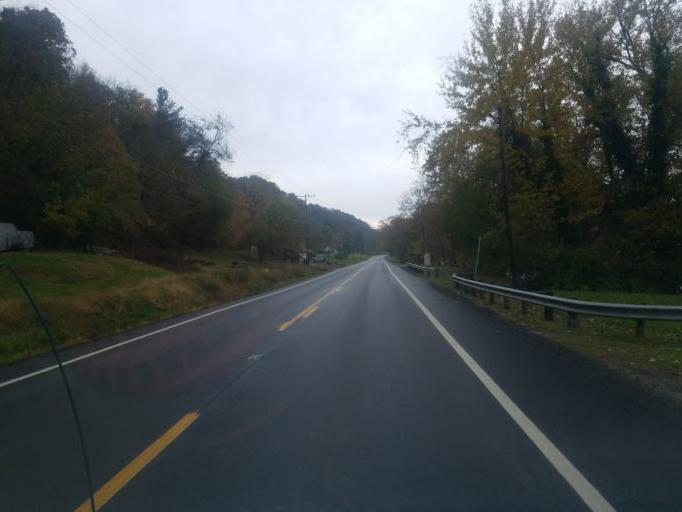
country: US
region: Ohio
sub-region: Washington County
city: Beverly
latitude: 39.5645
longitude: -81.5723
